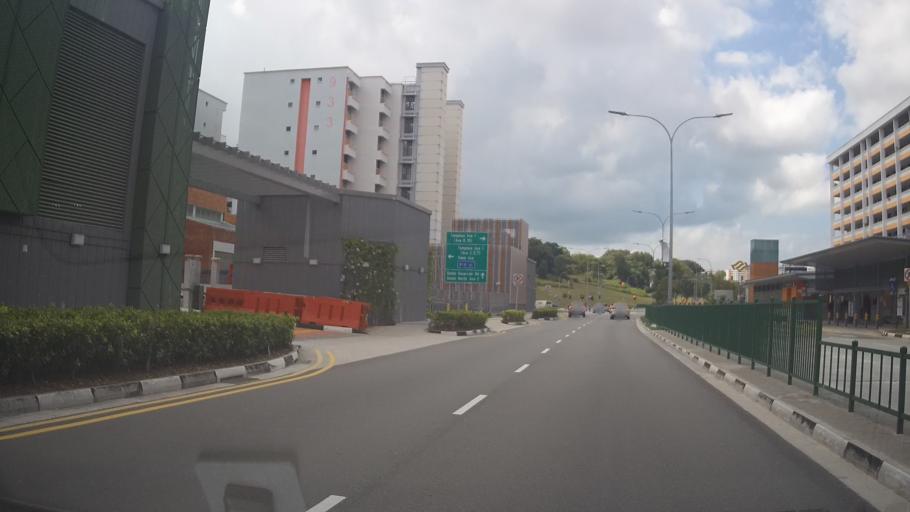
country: SG
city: Singapore
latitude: 1.3464
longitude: 103.9384
